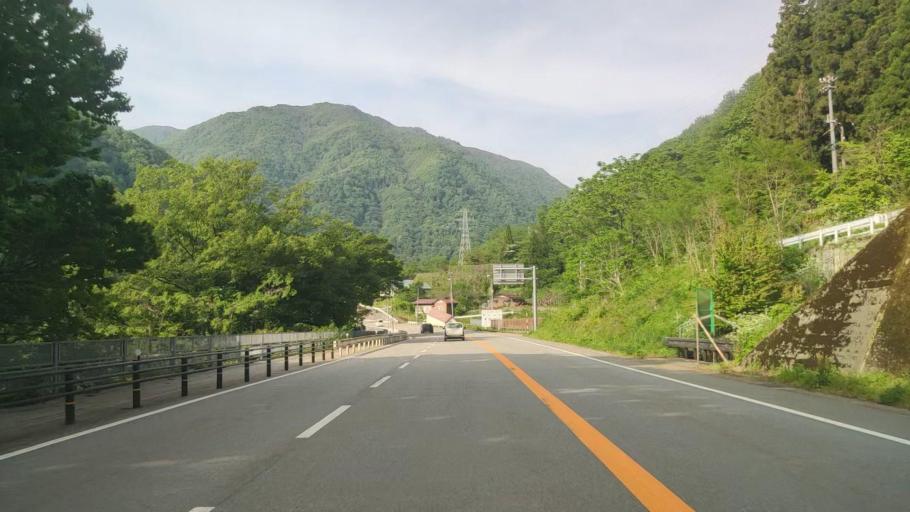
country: JP
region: Toyama
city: Yatsuomachi-higashikumisaka
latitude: 36.3980
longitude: 137.2879
